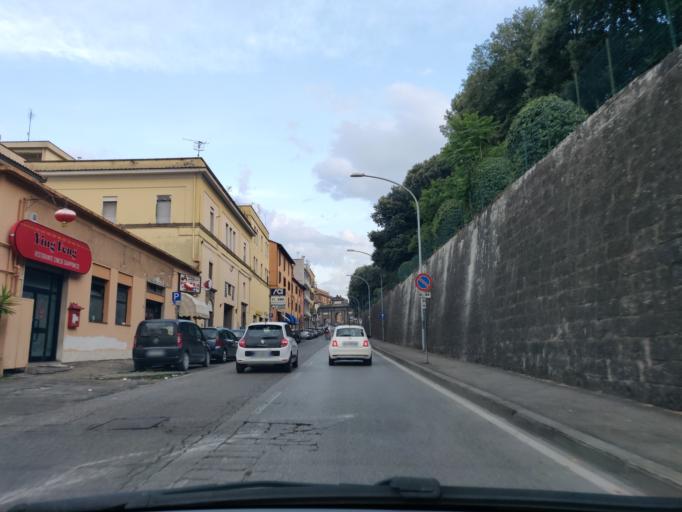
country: IT
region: Latium
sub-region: Provincia di Viterbo
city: Viterbo
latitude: 42.4237
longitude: 12.1023
